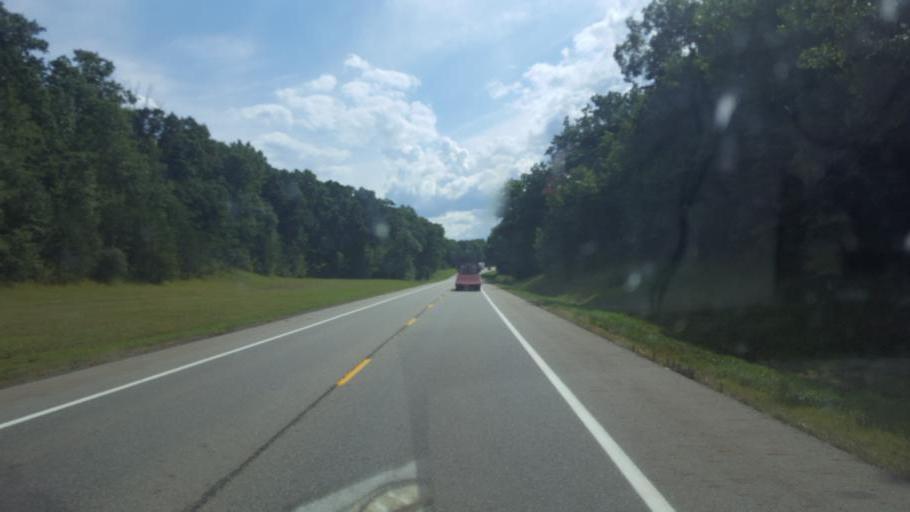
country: US
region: Ohio
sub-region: Portage County
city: Ravenna
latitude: 41.1327
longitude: -81.2294
